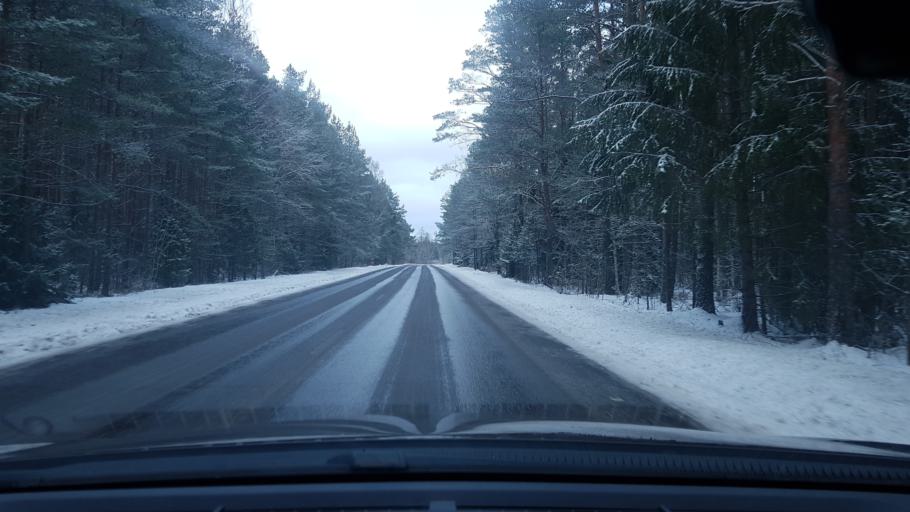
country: EE
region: Harju
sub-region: Keila linn
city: Keila
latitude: 59.3308
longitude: 24.2748
